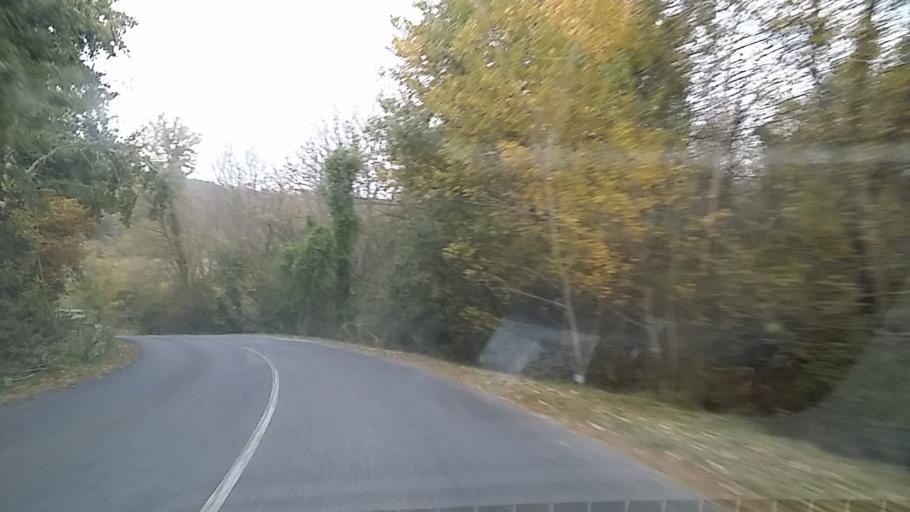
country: HU
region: Veszprem
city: Herend
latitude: 47.2508
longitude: 17.7449
